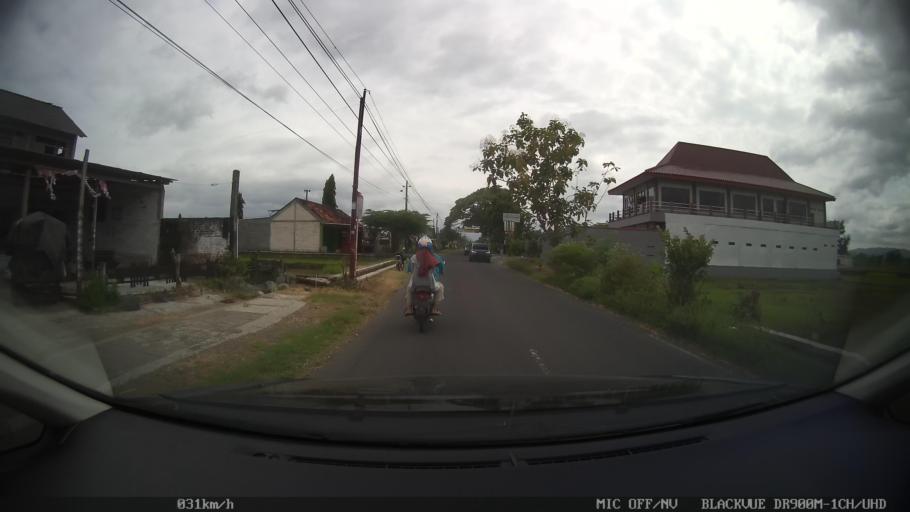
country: ID
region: Daerah Istimewa Yogyakarta
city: Depok
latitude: -7.8219
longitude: 110.4425
